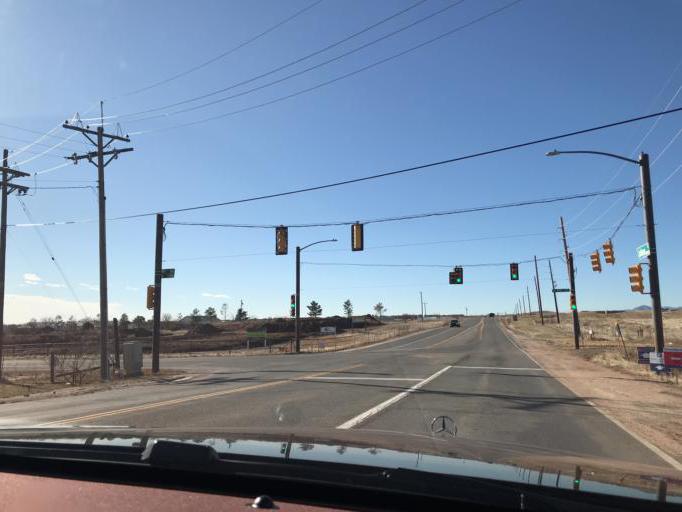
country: US
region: Colorado
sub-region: Boulder County
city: Superior
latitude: 39.8712
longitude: -105.1655
